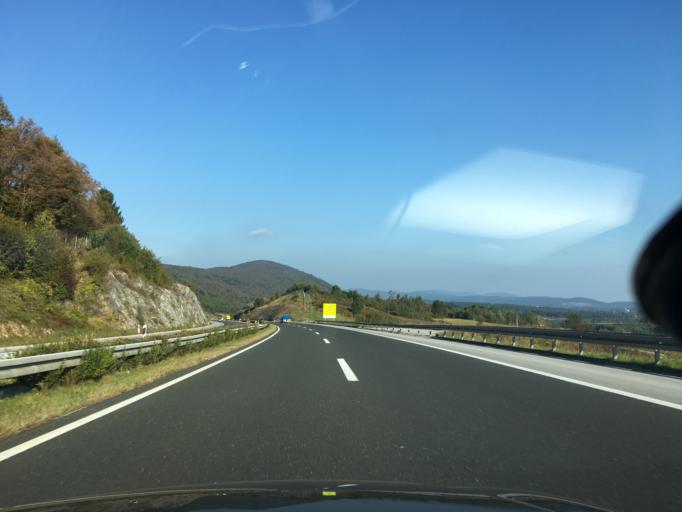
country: HR
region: Karlovacka
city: Ostarije
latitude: 45.1774
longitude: 15.2772
